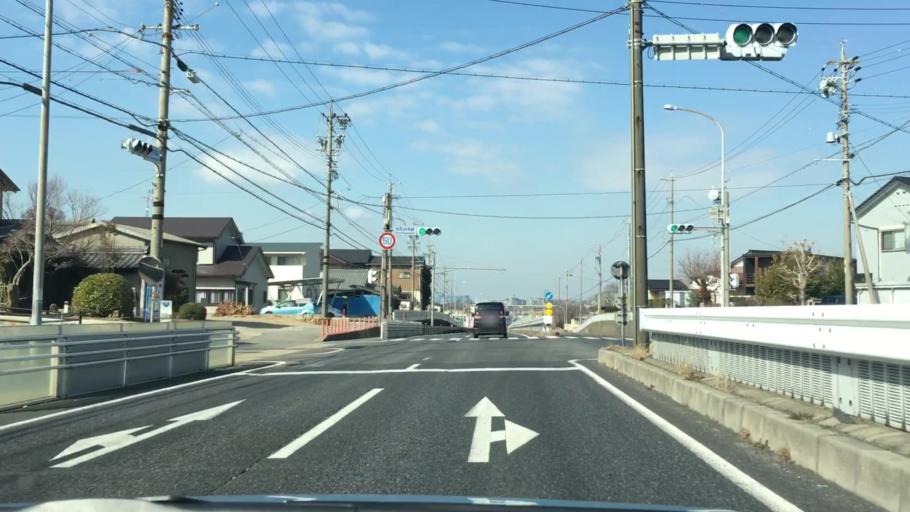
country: JP
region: Aichi
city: Okazaki
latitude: 34.9222
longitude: 137.2049
